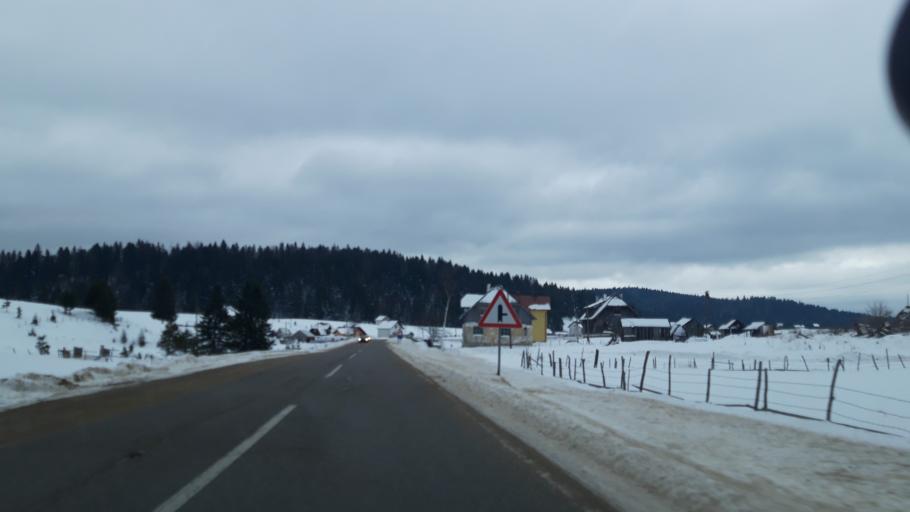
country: BA
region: Republika Srpska
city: Han Pijesak
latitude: 44.1090
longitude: 18.9690
